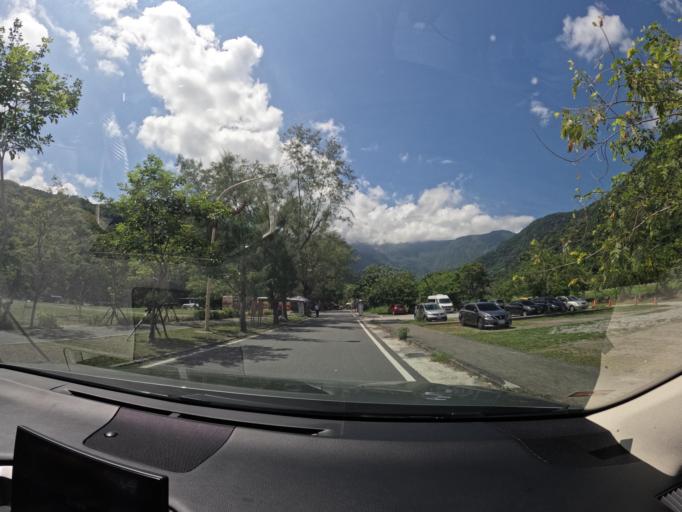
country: TW
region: Taiwan
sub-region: Hualien
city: Hualian
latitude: 23.7189
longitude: 121.4037
